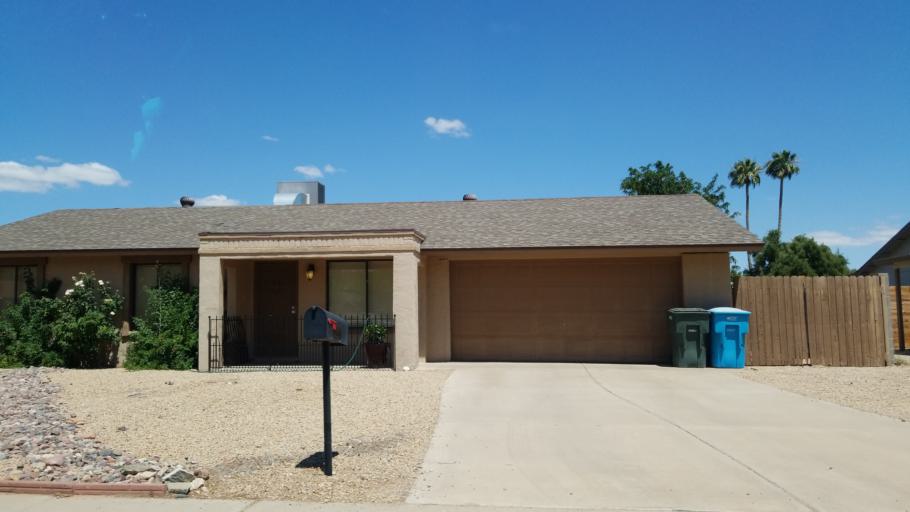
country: US
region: Arizona
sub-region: Maricopa County
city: Paradise Valley
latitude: 33.6069
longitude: -112.0176
